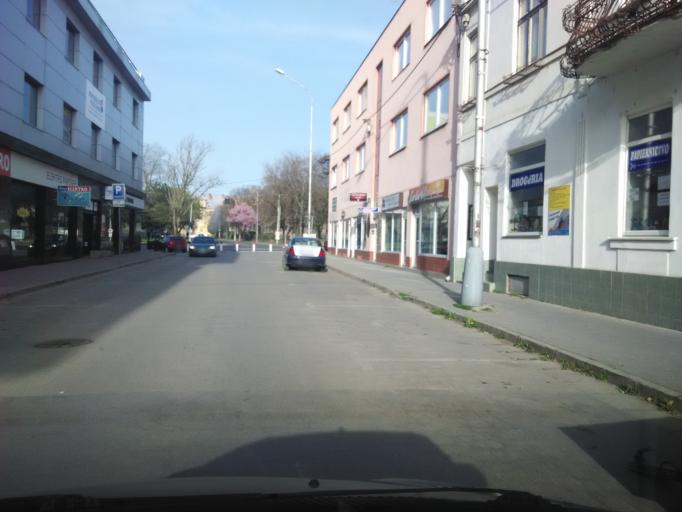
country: SK
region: Nitriansky
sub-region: Okres Nove Zamky
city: Nove Zamky
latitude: 47.9890
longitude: 18.1700
